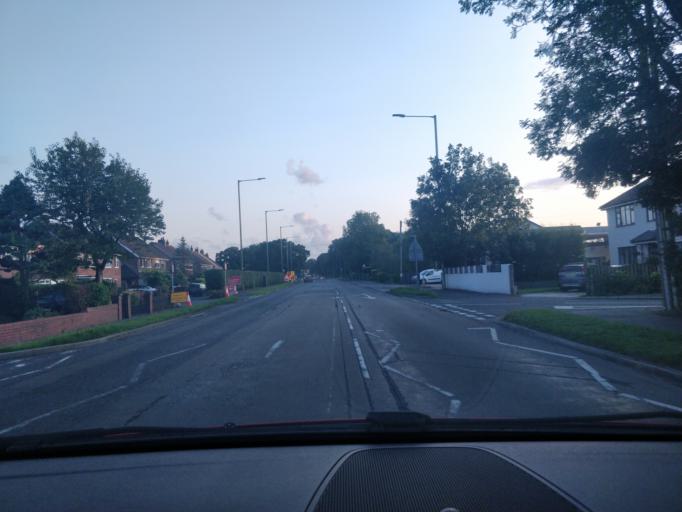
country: GB
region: England
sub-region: Lancashire
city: Preston
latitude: 53.7432
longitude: -2.7452
